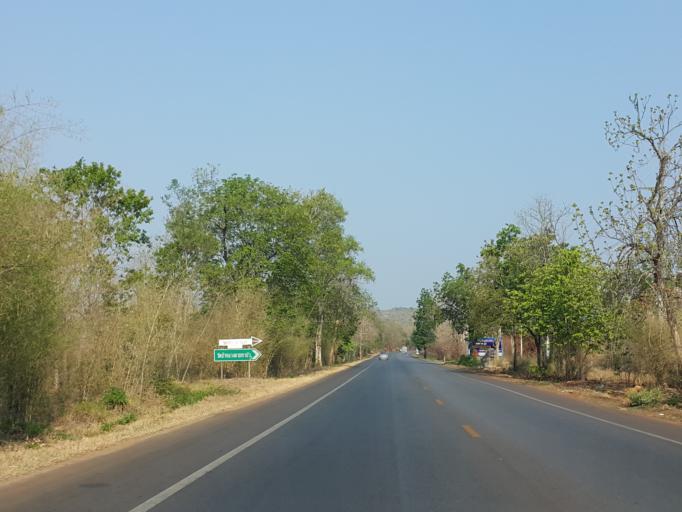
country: TH
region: Kanchanaburi
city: Sai Yok
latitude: 14.0980
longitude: 99.2400
